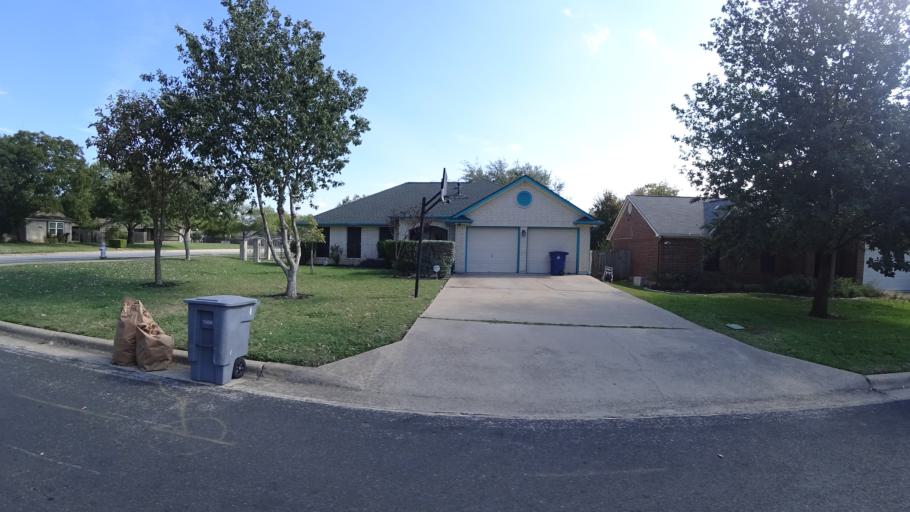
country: US
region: Texas
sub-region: Travis County
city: Shady Hollow
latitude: 30.1989
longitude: -97.8247
